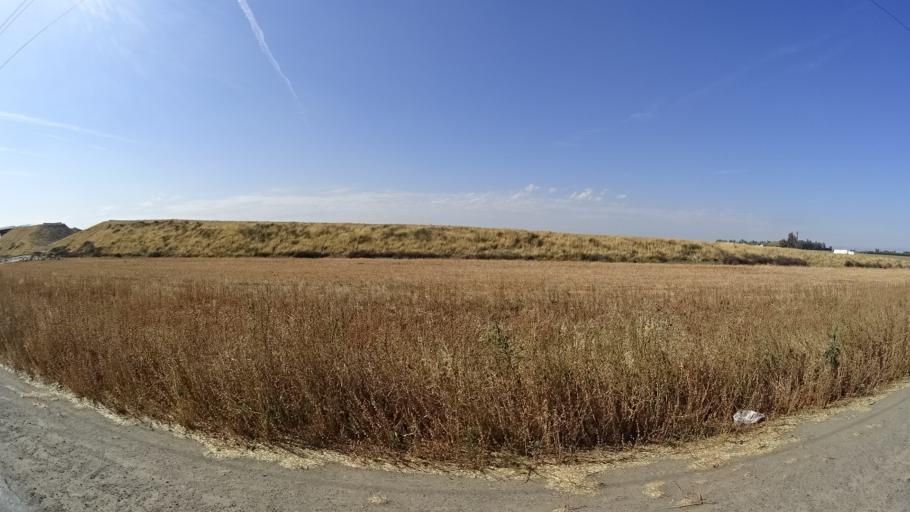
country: US
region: California
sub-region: Kings County
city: Home Garden
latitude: 36.2259
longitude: -119.6096
